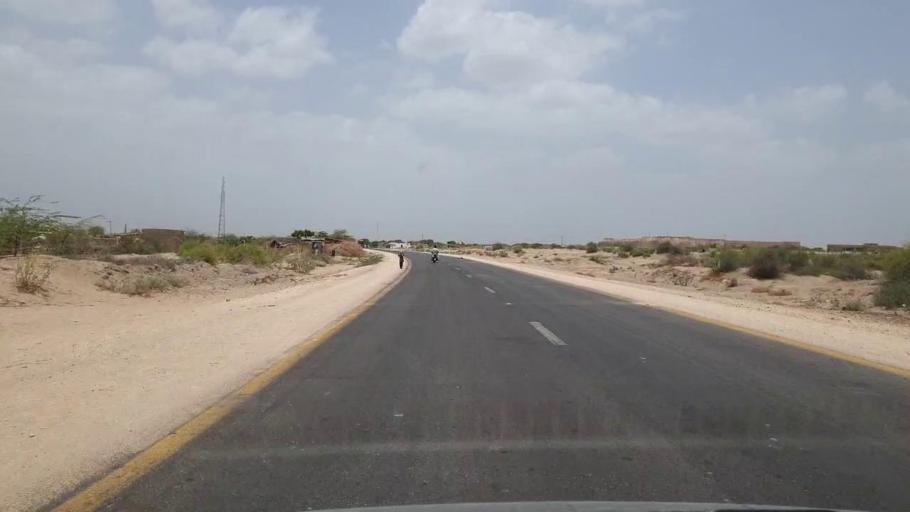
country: PK
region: Sindh
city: Naukot
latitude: 24.8416
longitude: 69.4546
